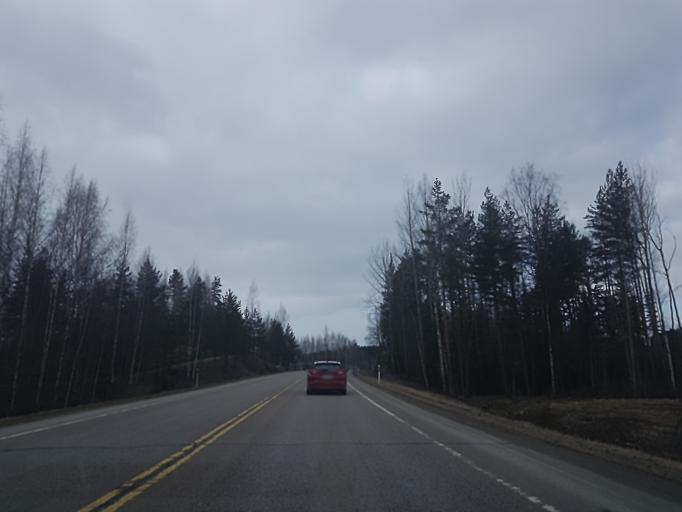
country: FI
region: South Karelia
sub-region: Imatra
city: Parikkala
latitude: 61.4911
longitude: 29.4839
